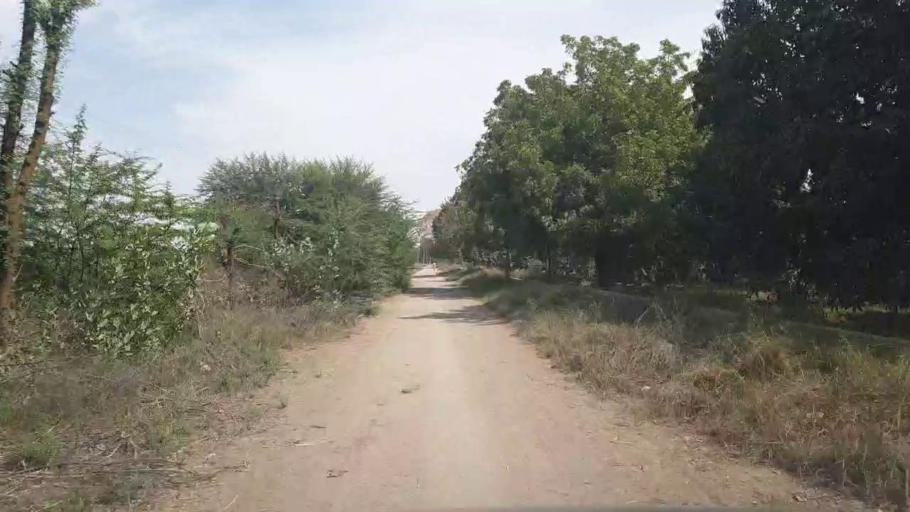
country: PK
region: Sindh
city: Kunri
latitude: 25.2172
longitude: 69.6896
